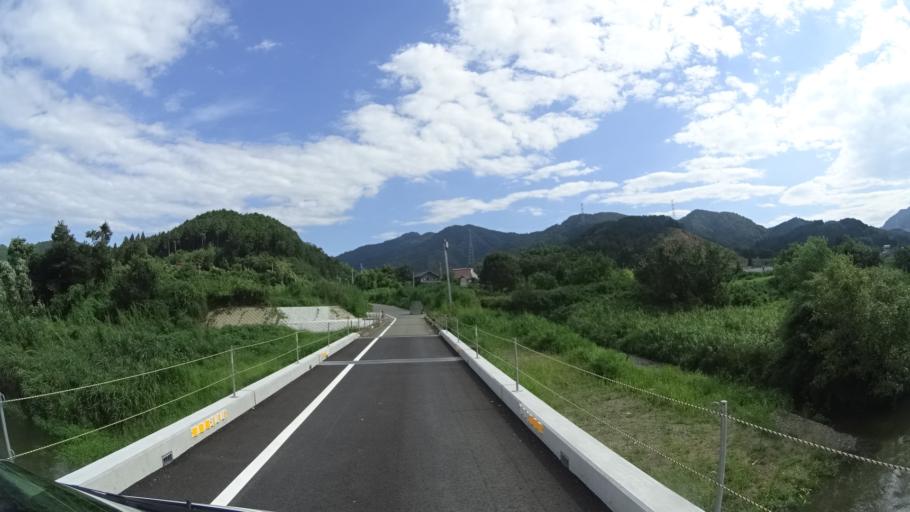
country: JP
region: Kyoto
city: Fukuchiyama
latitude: 35.3695
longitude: 135.1294
